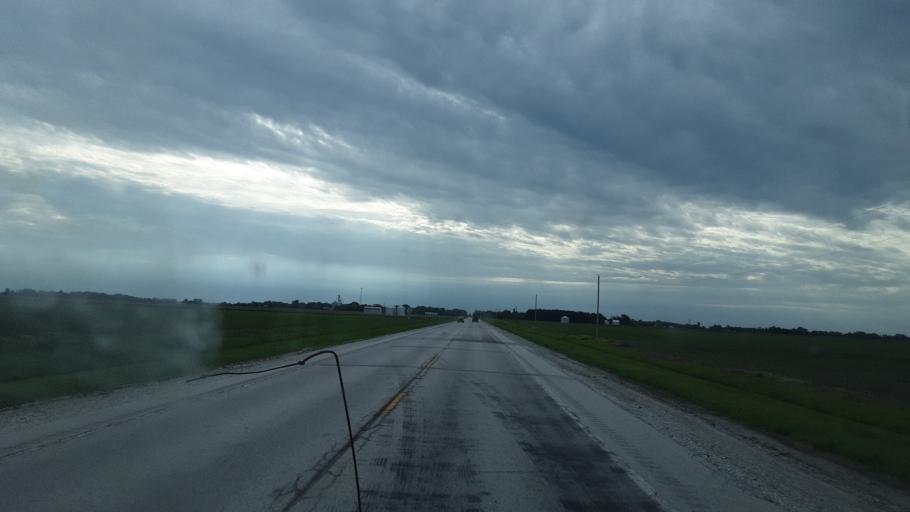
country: US
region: Illinois
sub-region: Hancock County
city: Hamilton
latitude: 40.3953
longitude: -91.2719
